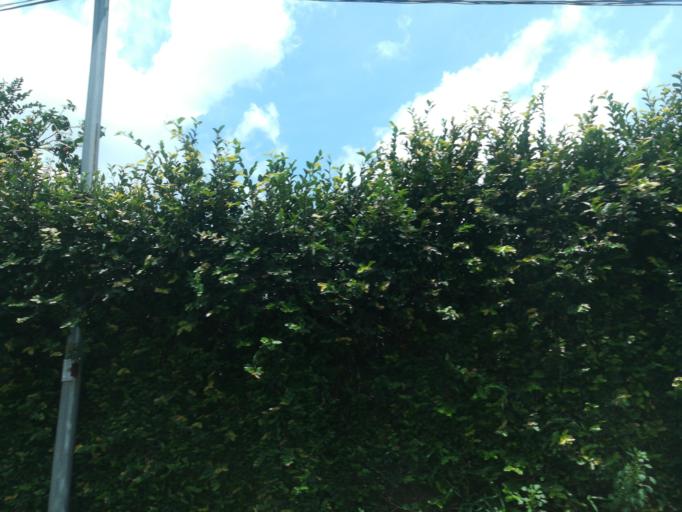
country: NG
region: Lagos
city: Somolu
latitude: 6.5413
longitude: 3.3636
